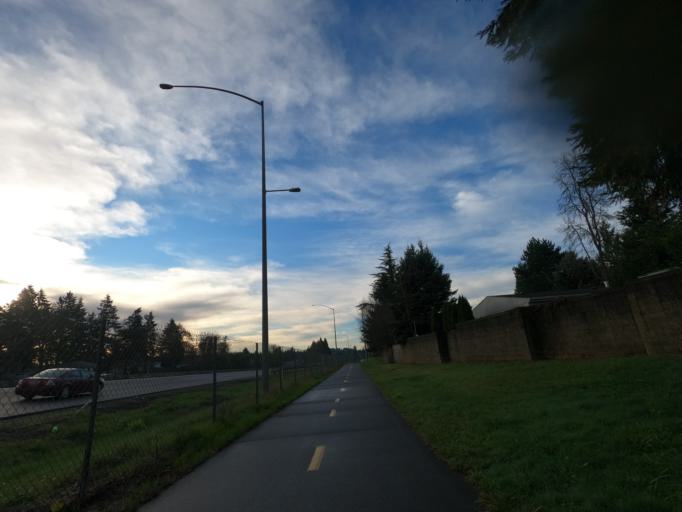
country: US
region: Oregon
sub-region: Clackamas County
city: Clackamas
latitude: 45.4038
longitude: -122.5722
